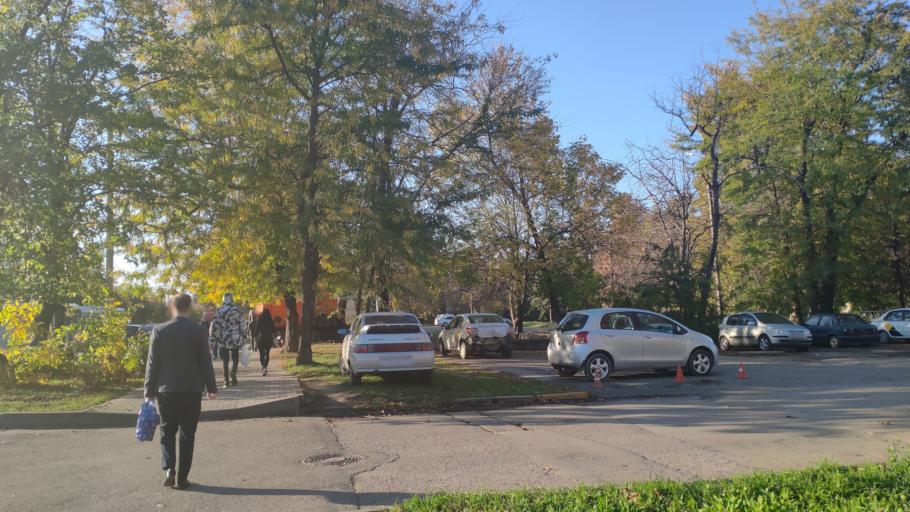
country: RU
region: Krasnodarskiy
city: Krasnodar
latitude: 45.0774
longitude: 39.0006
